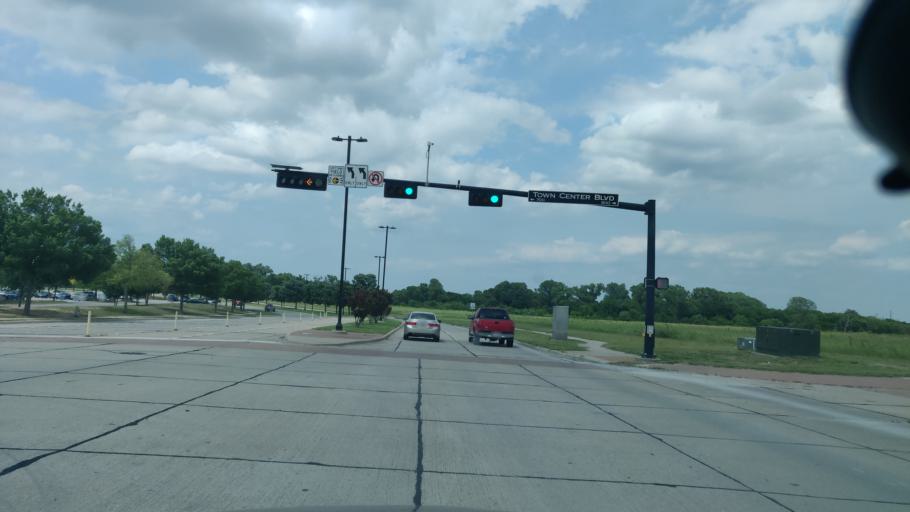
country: US
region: Texas
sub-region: Dallas County
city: Sachse
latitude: 32.9501
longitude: -96.6087
